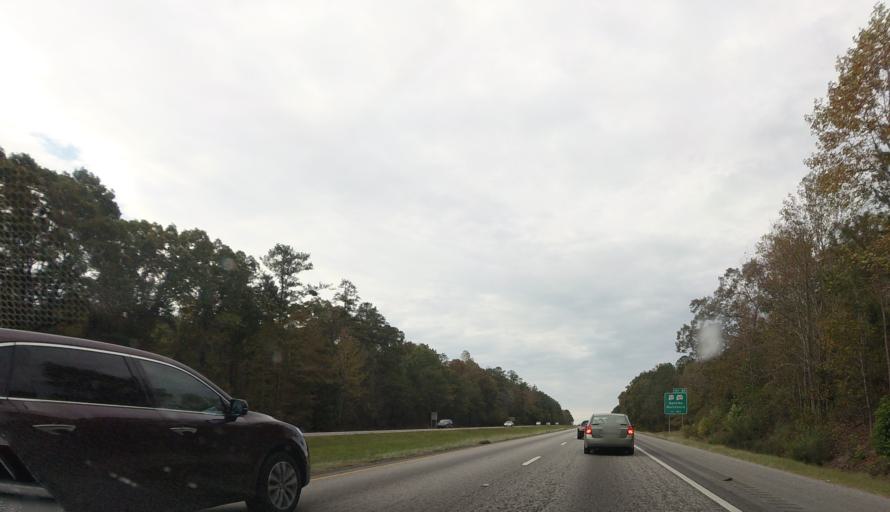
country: US
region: Alabama
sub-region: Lee County
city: Opelika
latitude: 32.6374
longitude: -85.3616
